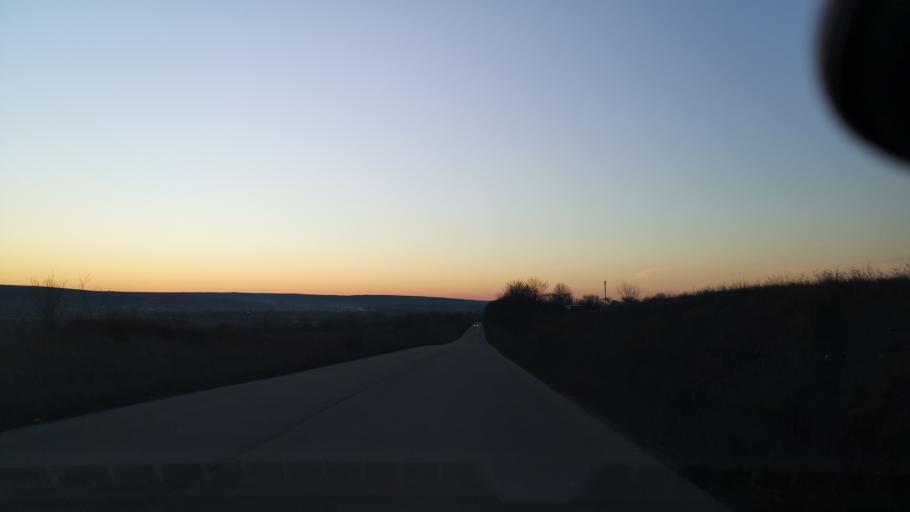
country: MD
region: Anenii Noi
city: Anenii Noi
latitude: 46.8889
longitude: 29.2763
